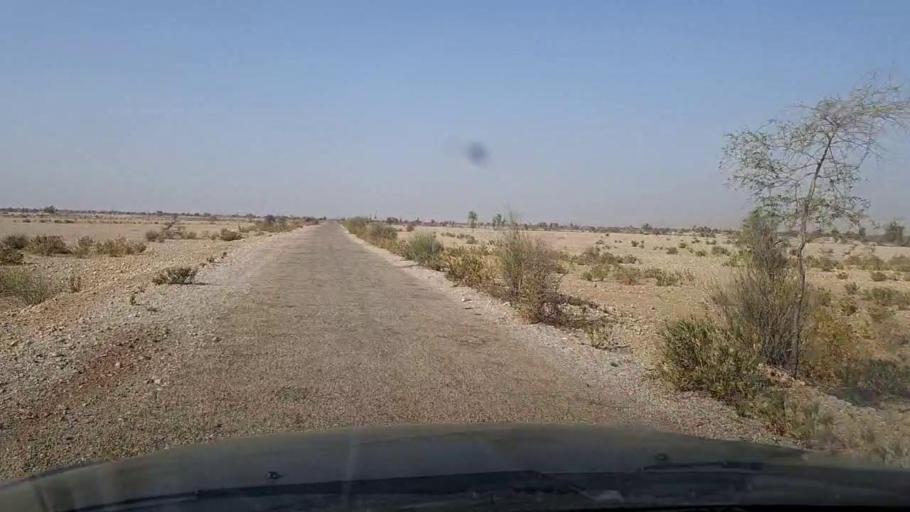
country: PK
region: Sindh
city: Sann
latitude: 25.9208
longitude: 68.0152
